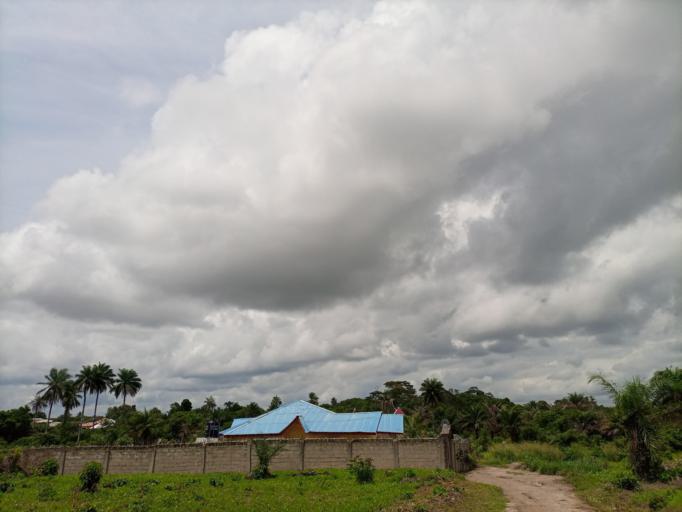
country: SL
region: Southern Province
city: Bo
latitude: 7.9766
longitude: -11.7698
